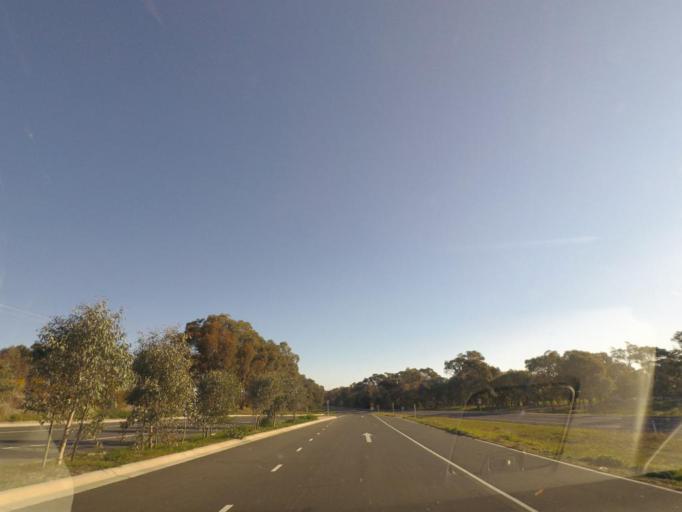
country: AU
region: Victoria
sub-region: Greater Shepparton
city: Shepparton
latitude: -36.7819
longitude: 145.5001
